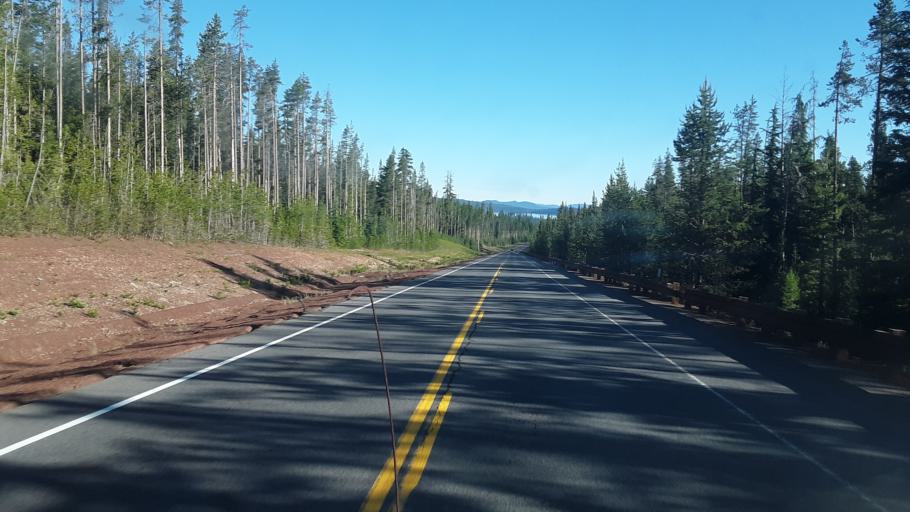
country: US
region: Oregon
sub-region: Lane County
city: Oakridge
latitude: 43.1079
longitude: -122.1299
